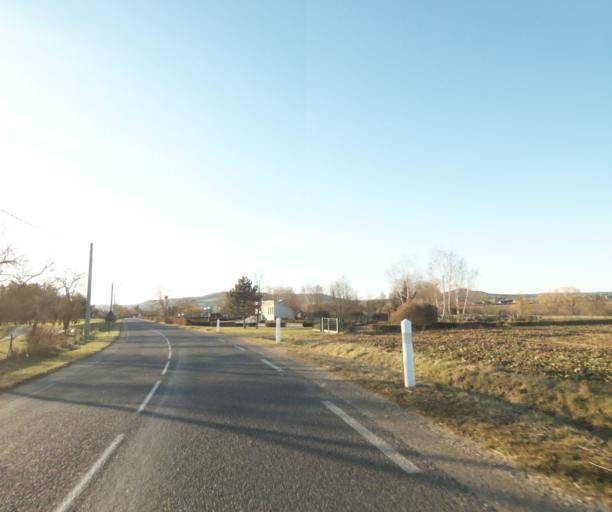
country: FR
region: Lorraine
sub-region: Departement de Meurthe-et-Moselle
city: Seichamps
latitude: 48.7038
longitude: 6.2705
